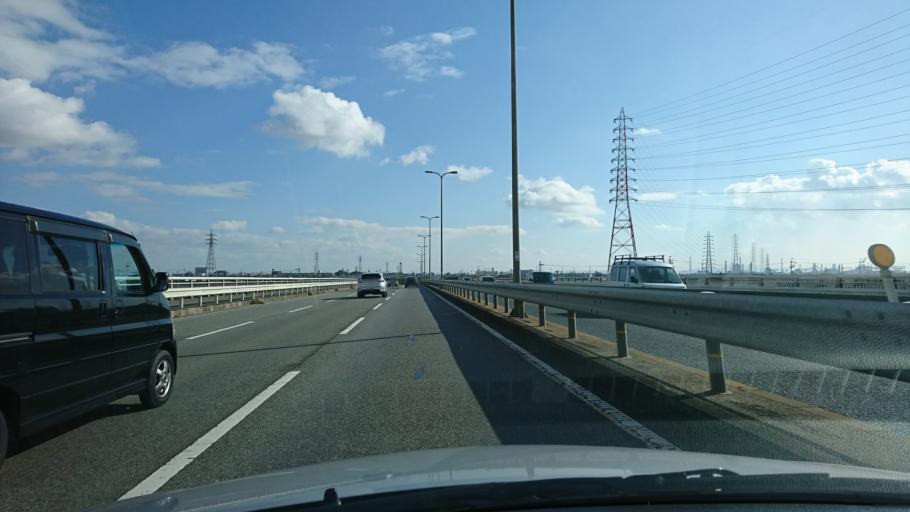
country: JP
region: Hyogo
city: Kakogawacho-honmachi
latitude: 34.7651
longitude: 134.8107
